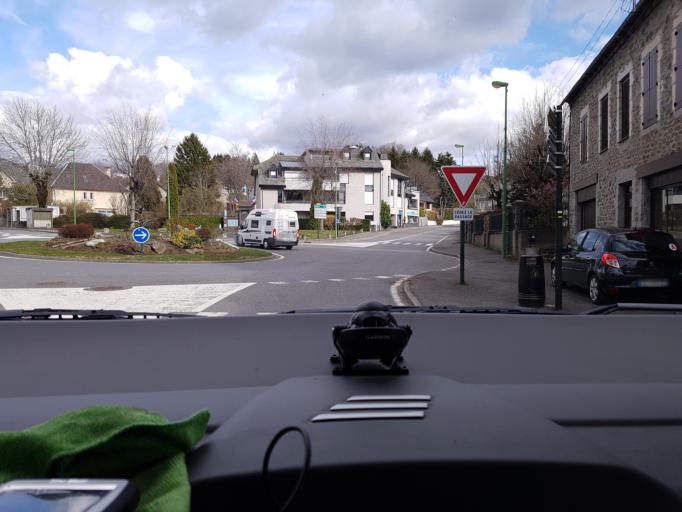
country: FR
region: Midi-Pyrenees
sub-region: Departement de l'Aveyron
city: Laguiole
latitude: 44.6831
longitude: 2.8507
